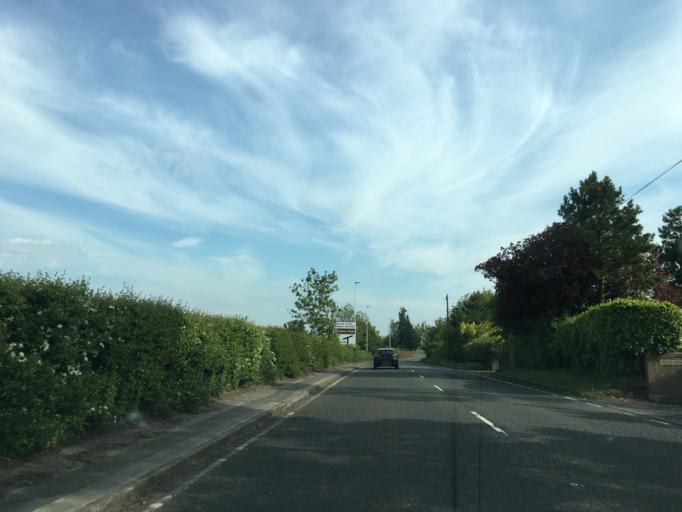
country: GB
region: Scotland
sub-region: Midlothian
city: Loanhead
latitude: 55.8645
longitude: -3.1856
